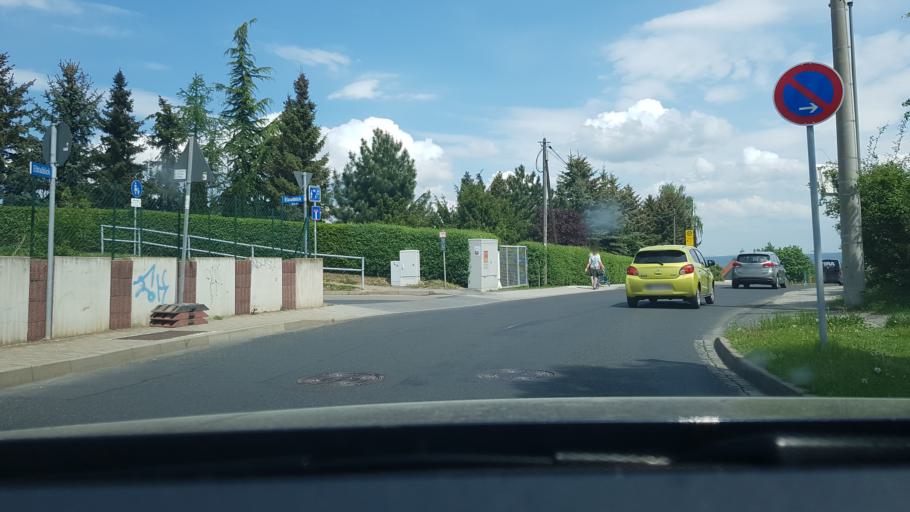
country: DE
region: Saxony
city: Freital
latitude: 51.0306
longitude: 13.6621
